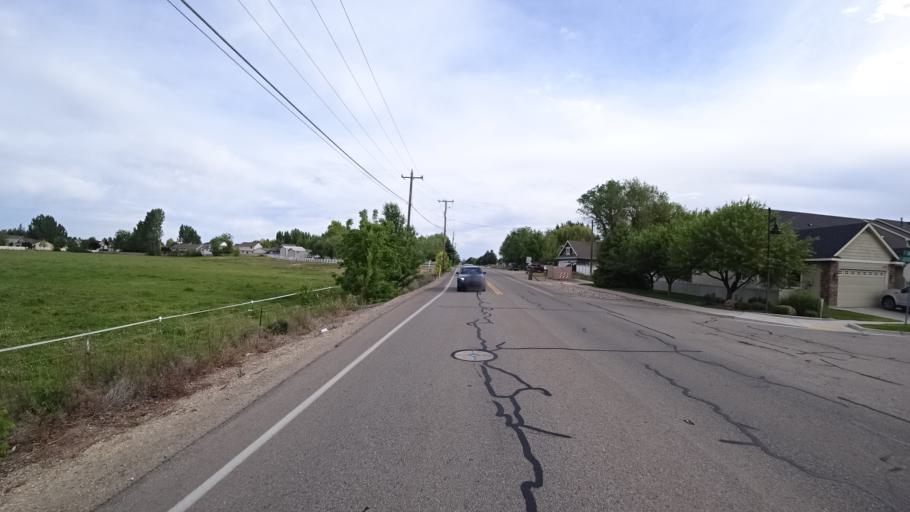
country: US
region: Idaho
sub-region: Ada County
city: Meridian
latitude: 43.5768
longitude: -116.3747
